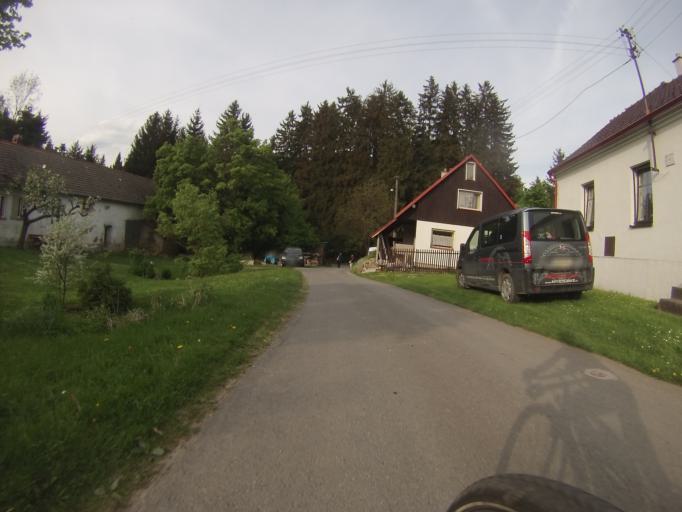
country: CZ
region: Olomoucky
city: Protivanov
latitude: 49.4666
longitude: 16.8785
